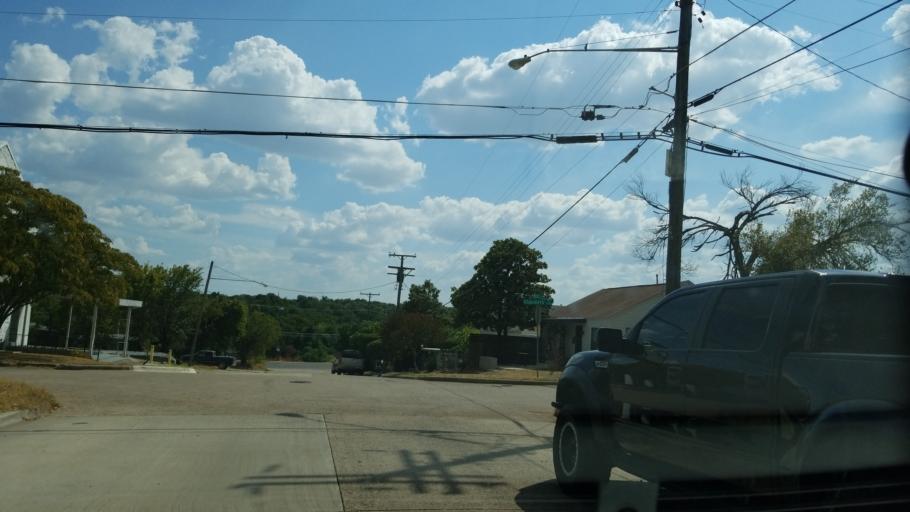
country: US
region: Texas
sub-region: Dallas County
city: Dallas
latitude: 32.7686
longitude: -96.8401
